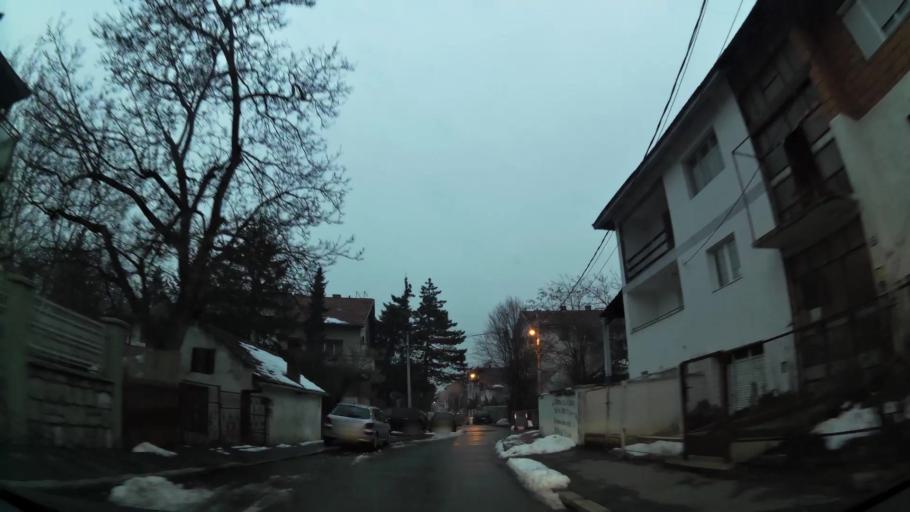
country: RS
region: Central Serbia
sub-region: Belgrade
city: Vozdovac
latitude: 44.7739
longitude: 20.4879
